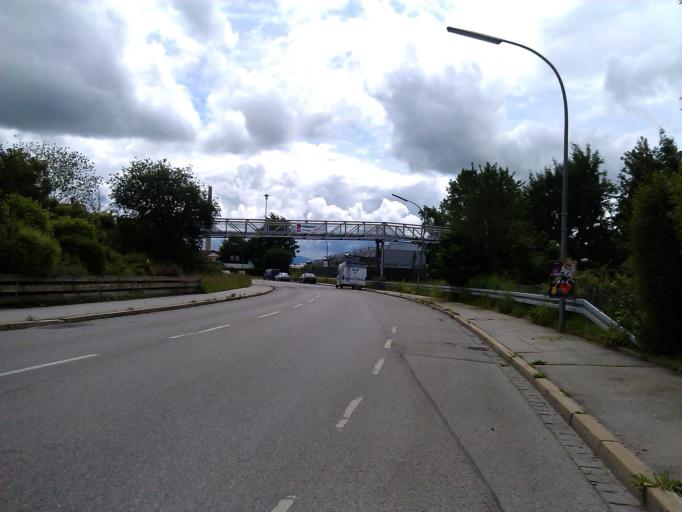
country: DE
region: Bavaria
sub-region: Swabia
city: Marktoberdorf
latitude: 47.7880
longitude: 10.6156
